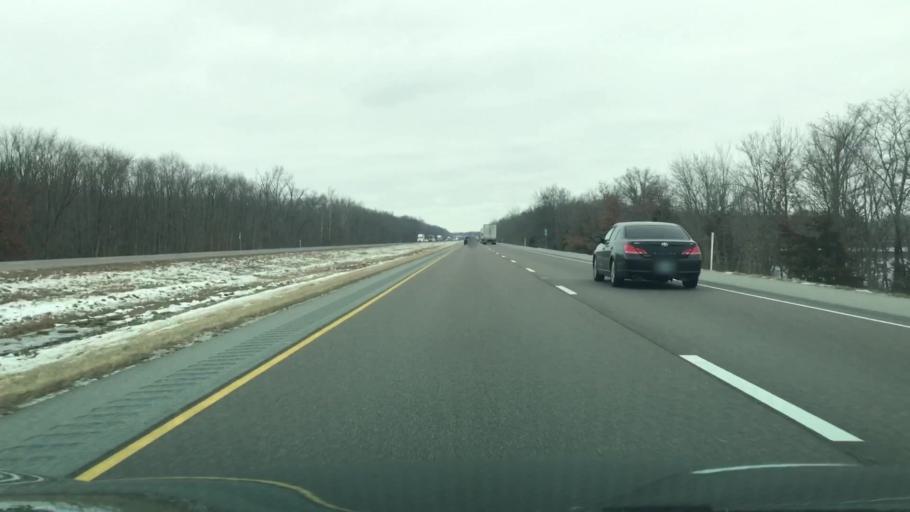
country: US
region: Illinois
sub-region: Jefferson County
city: Ina
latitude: 38.2284
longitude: -88.9058
